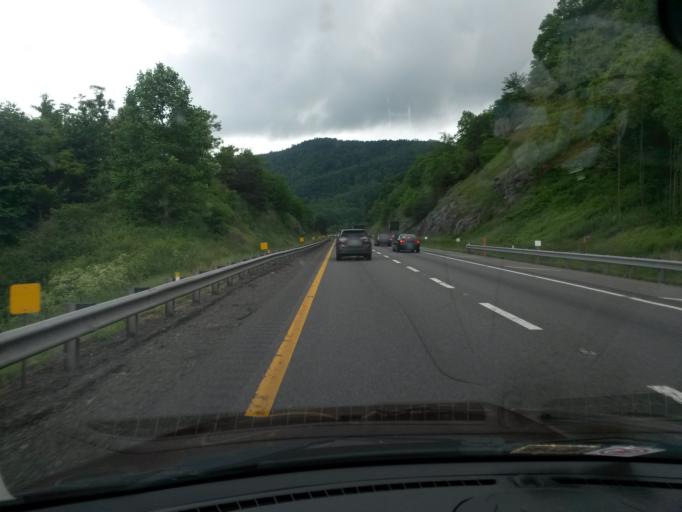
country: US
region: Virginia
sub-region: Carroll County
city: Cana
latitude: 36.6242
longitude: -80.7328
